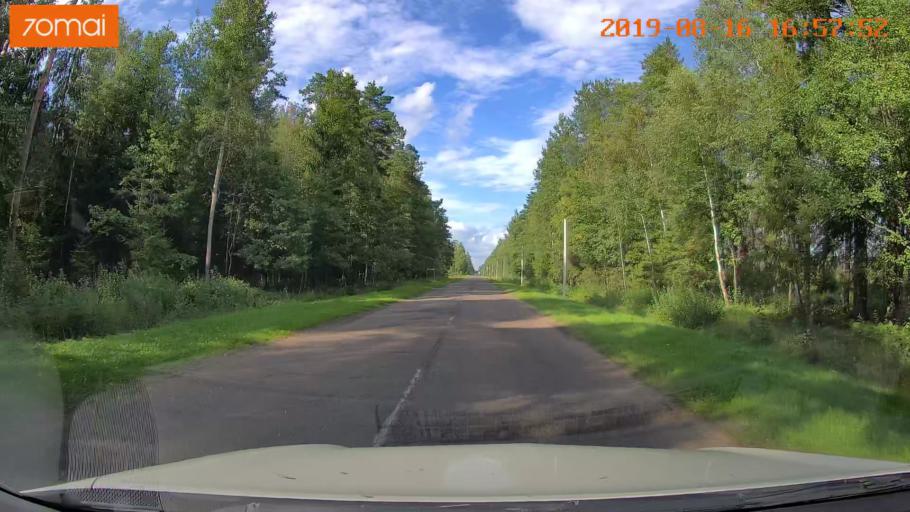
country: BY
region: Mogilev
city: Hlusha
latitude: 53.2618
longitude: 28.8283
